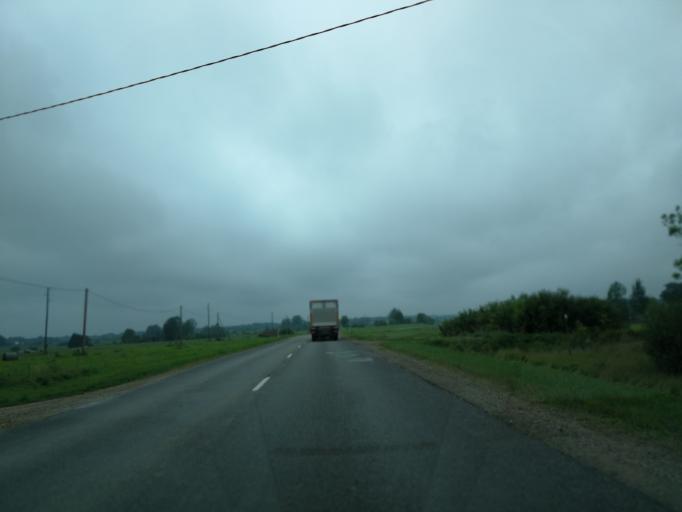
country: LV
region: Livani
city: Livani
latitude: 56.3469
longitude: 26.2843
